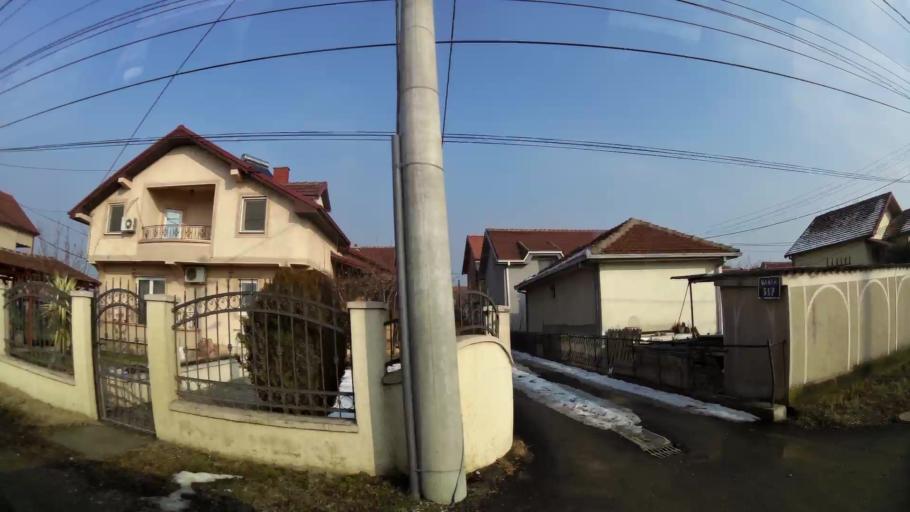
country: MK
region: Ilinden
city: Marino
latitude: 41.9842
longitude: 21.5904
